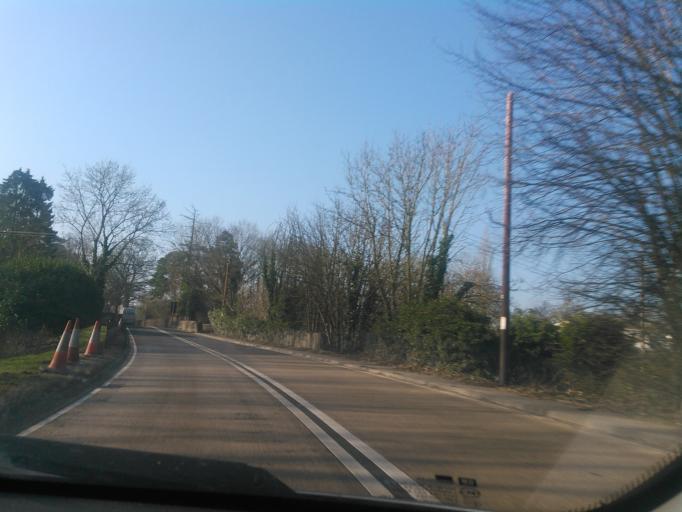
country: GB
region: England
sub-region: Shropshire
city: Craven Arms
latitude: 52.4576
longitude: -2.8364
